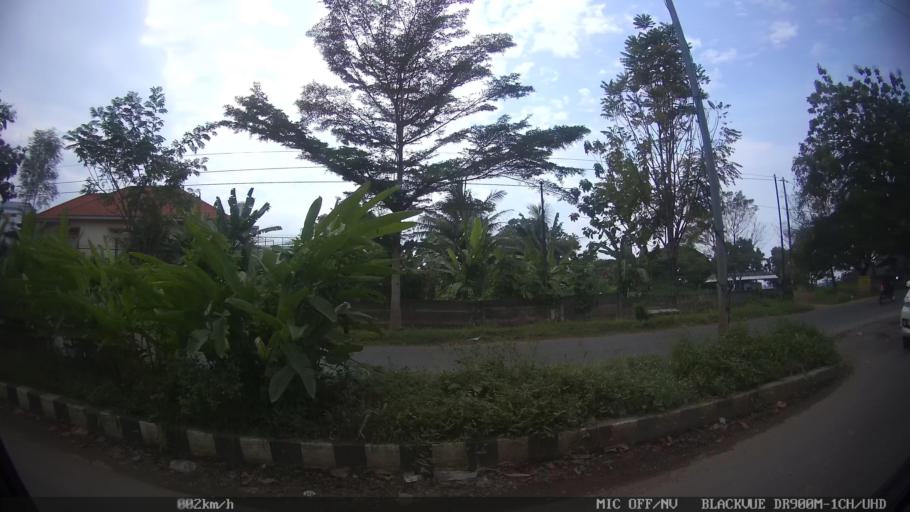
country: ID
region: Lampung
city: Bandarlampung
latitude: -5.4369
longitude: 105.2485
